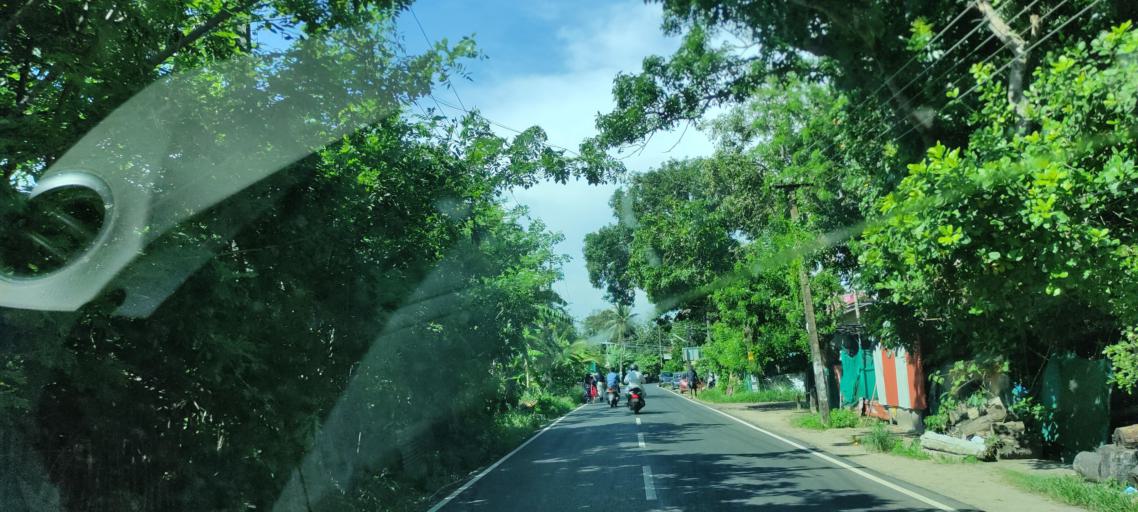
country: IN
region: Kerala
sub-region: Alappuzha
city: Mavelikara
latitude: 9.3145
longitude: 76.3866
